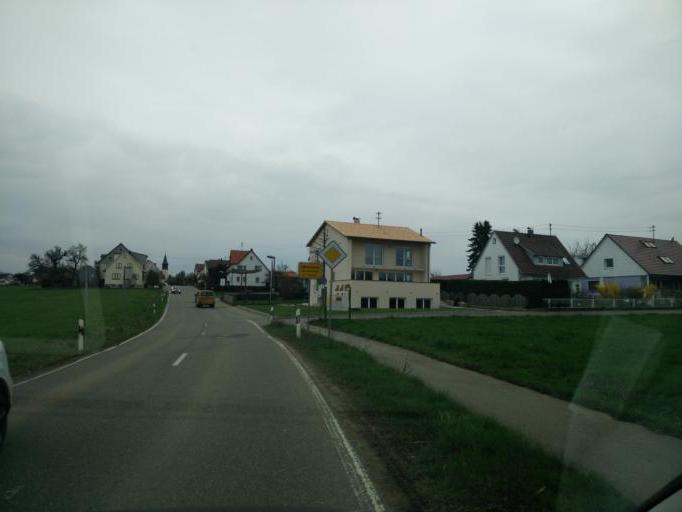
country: DE
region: Baden-Wuerttemberg
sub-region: Tuebingen Region
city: Gomaringen
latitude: 48.4755
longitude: 9.1030
